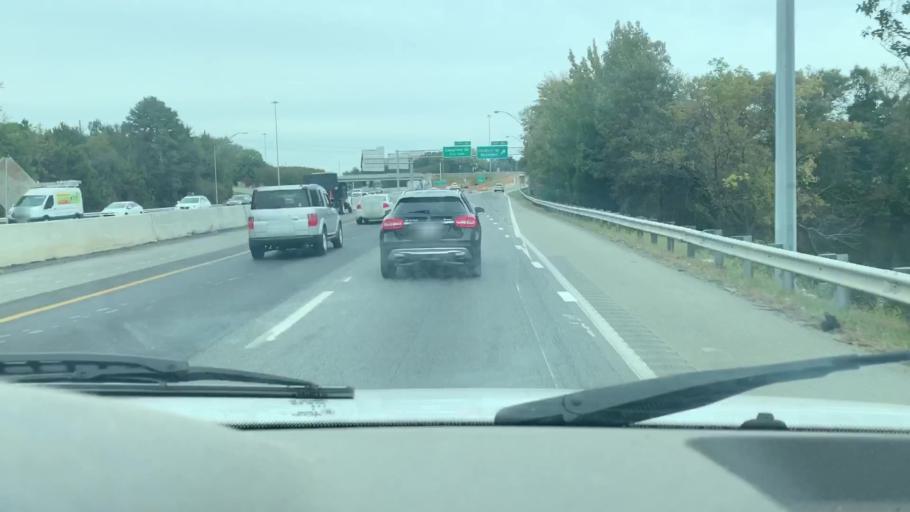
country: US
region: North Carolina
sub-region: Mecklenburg County
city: Cornelius
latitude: 35.5006
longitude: -80.8674
